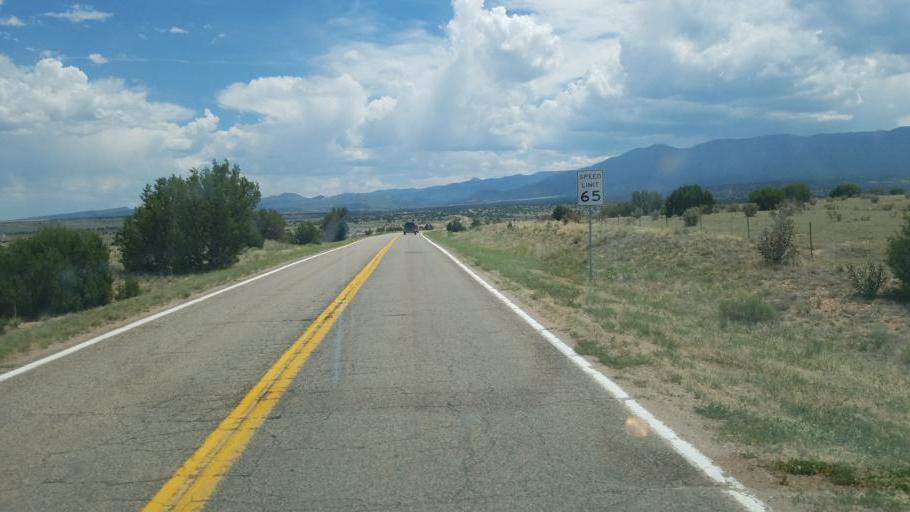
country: US
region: Colorado
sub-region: Fremont County
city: Florence
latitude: 38.3265
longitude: -105.1053
